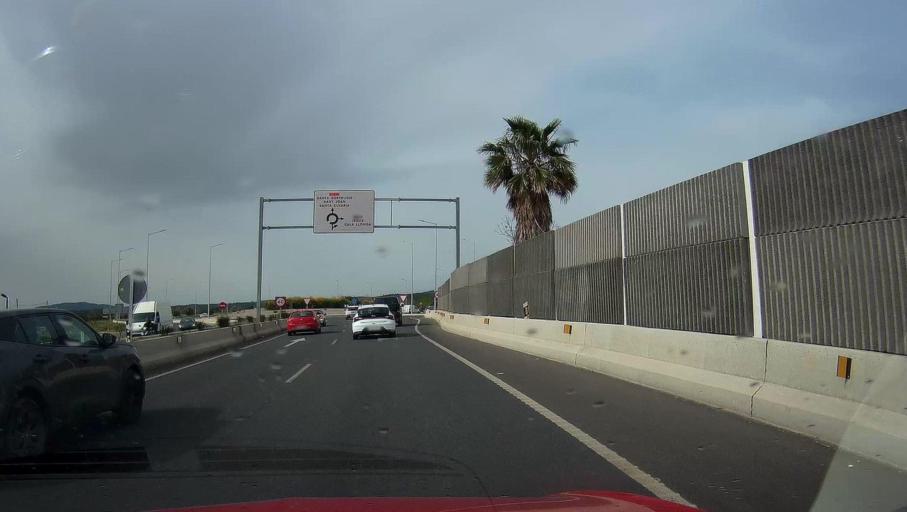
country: ES
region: Balearic Islands
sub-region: Illes Balears
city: Ibiza
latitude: 38.9342
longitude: 1.4444
